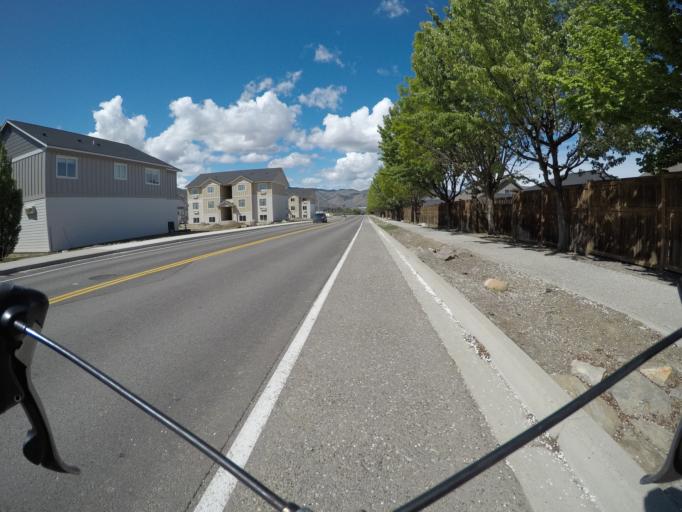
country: US
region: Washington
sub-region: Chelan County
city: South Wenatchee
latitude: 47.3986
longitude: -120.2631
